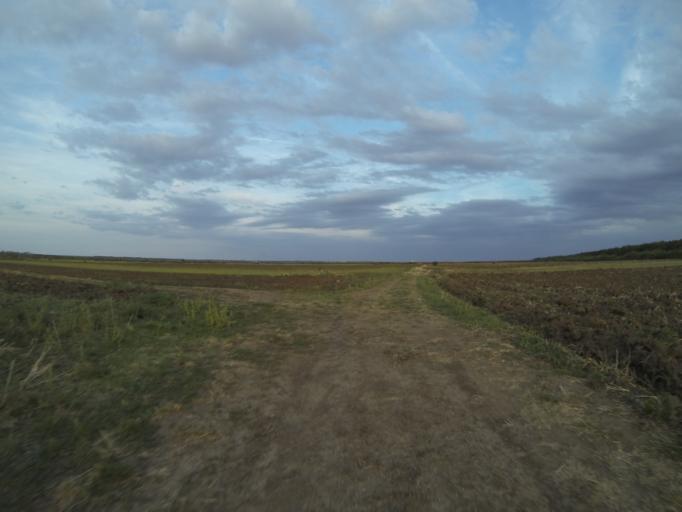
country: RO
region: Dolj
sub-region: Comuna Ceratu
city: Ceratu
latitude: 44.0936
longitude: 23.6748
